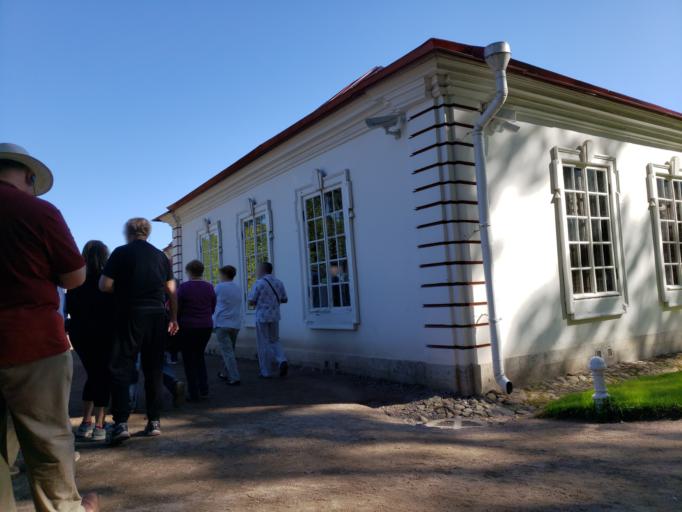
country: RU
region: St.-Petersburg
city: Peterhof
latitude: 59.8863
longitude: 29.9195
